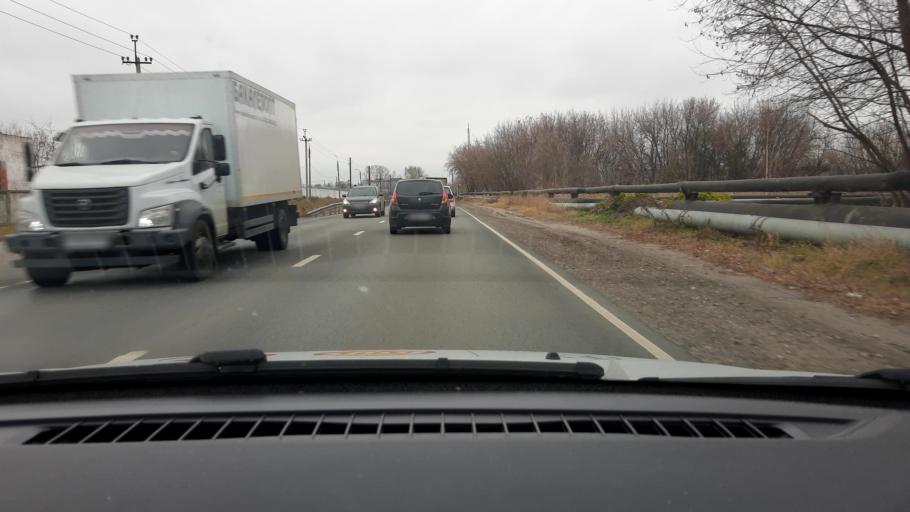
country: RU
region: Nizjnij Novgorod
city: Novaya Balakhna
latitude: 56.4966
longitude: 43.5942
